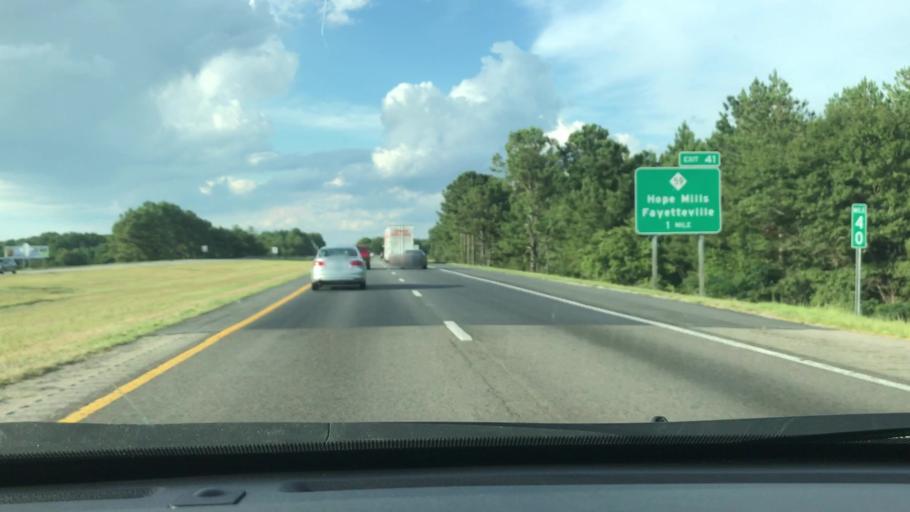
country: US
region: North Carolina
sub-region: Cumberland County
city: Hope Mills
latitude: 34.9278
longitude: -78.9409
